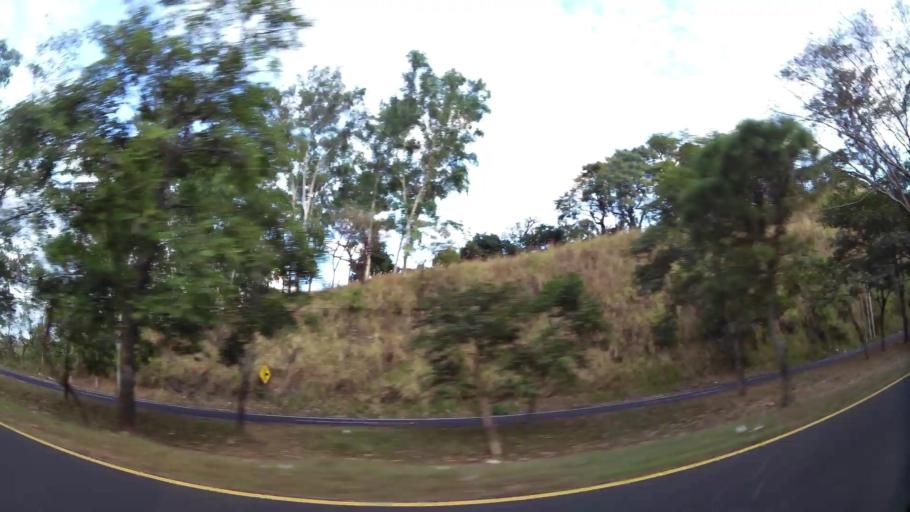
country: SV
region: San Vicente
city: San Sebastian
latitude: 13.7162
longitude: -88.8583
